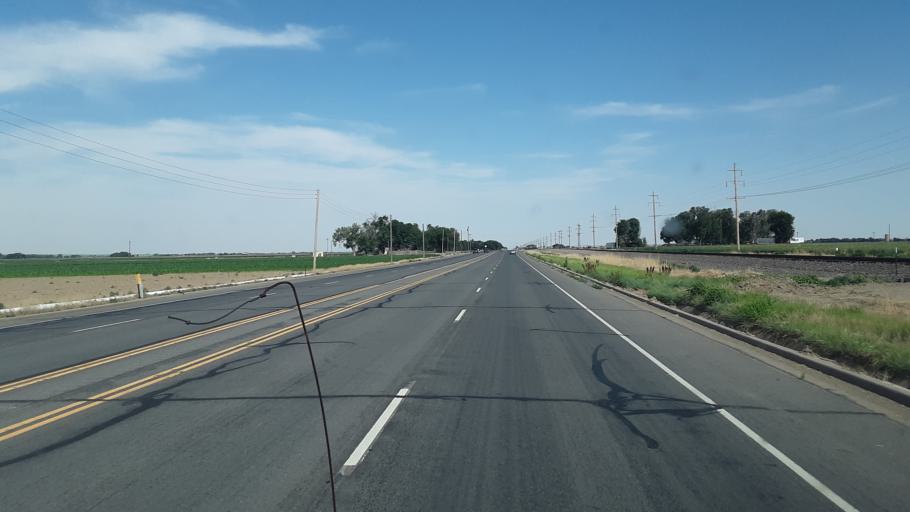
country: US
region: Colorado
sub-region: Otero County
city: Rocky Ford
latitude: 38.0954
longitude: -103.8254
